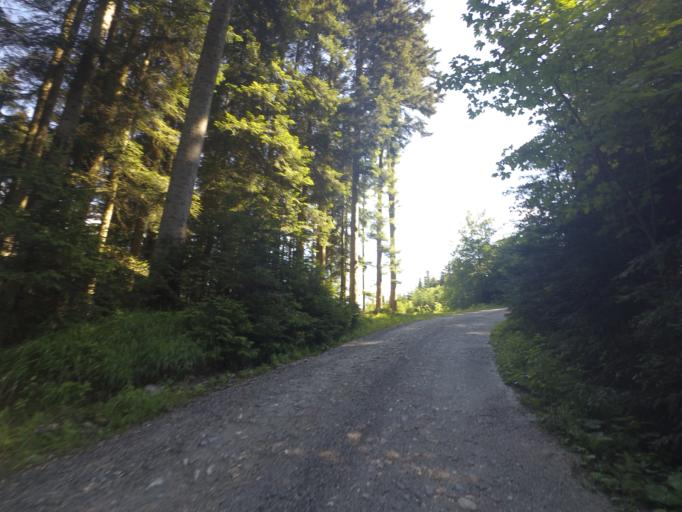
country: AT
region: Salzburg
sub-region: Politischer Bezirk Sankt Johann im Pongau
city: Schwarzach im Pongau
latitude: 47.3081
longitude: 13.1445
